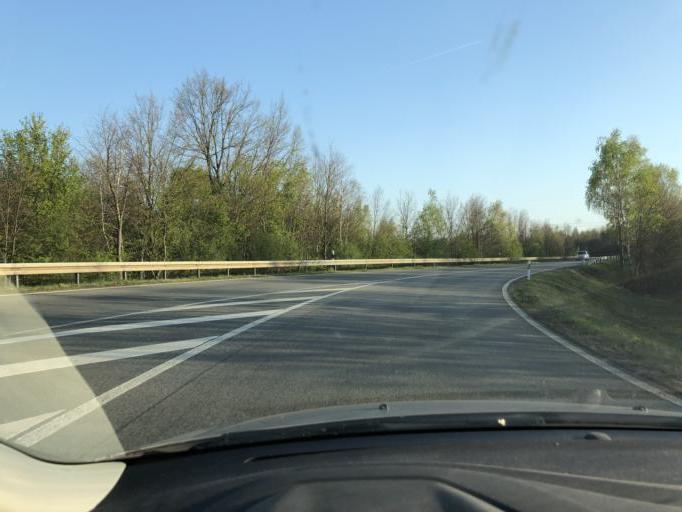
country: DE
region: Brandenburg
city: Ruhland
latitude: 51.4683
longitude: 13.8648
